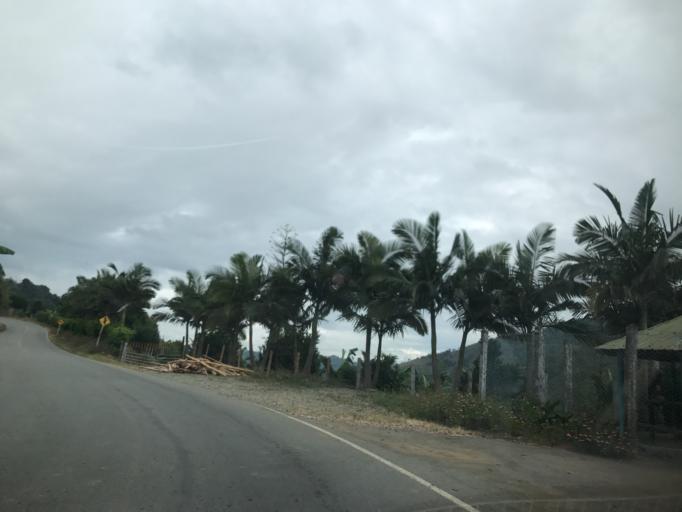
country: CO
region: Quindio
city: Genova
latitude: 4.2996
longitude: -75.7813
